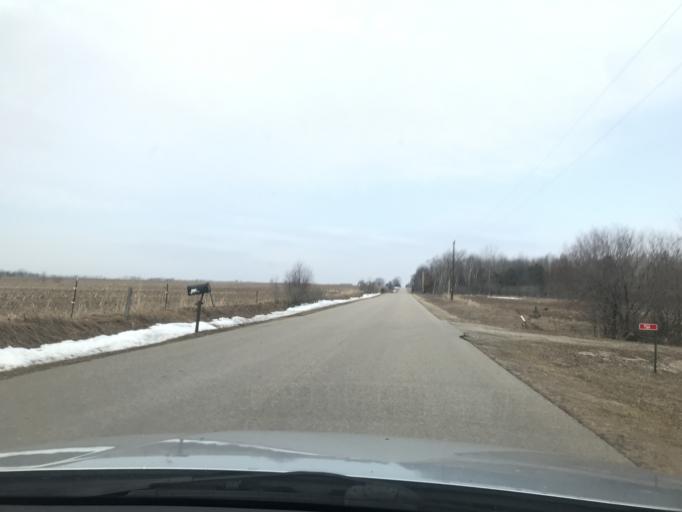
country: US
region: Wisconsin
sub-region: Oconto County
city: Oconto Falls
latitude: 44.8505
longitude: -88.1501
